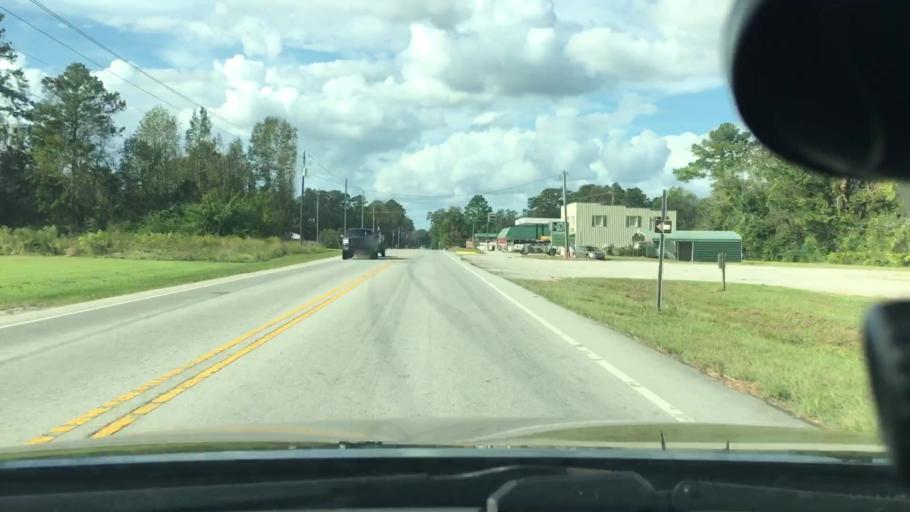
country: US
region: North Carolina
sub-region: Craven County
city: New Bern
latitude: 35.2189
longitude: -77.0653
